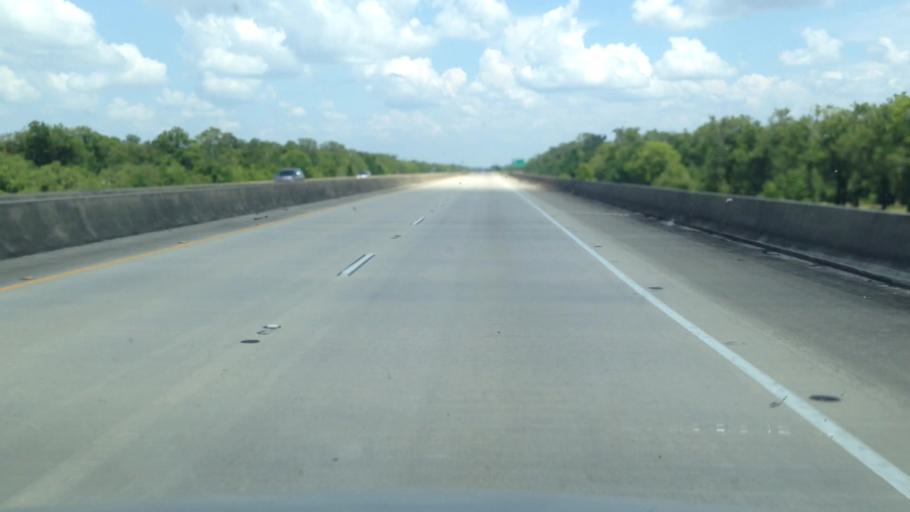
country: US
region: Louisiana
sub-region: Saint Landry Parish
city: Krotz Springs
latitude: 30.5477
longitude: -91.8275
